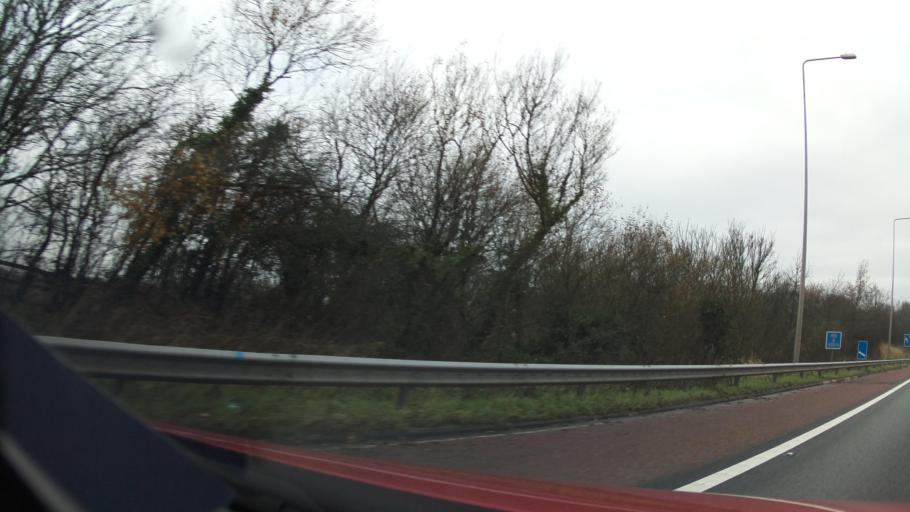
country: GB
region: England
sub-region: Lancashire
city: Coppull
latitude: 53.6265
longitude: -2.6886
